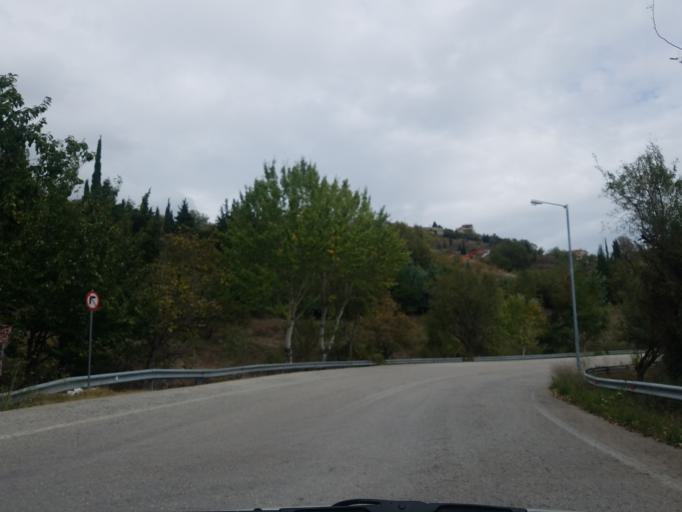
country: GR
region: Central Greece
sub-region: Nomos Voiotias
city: Arachova
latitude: 38.4830
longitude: 22.5771
